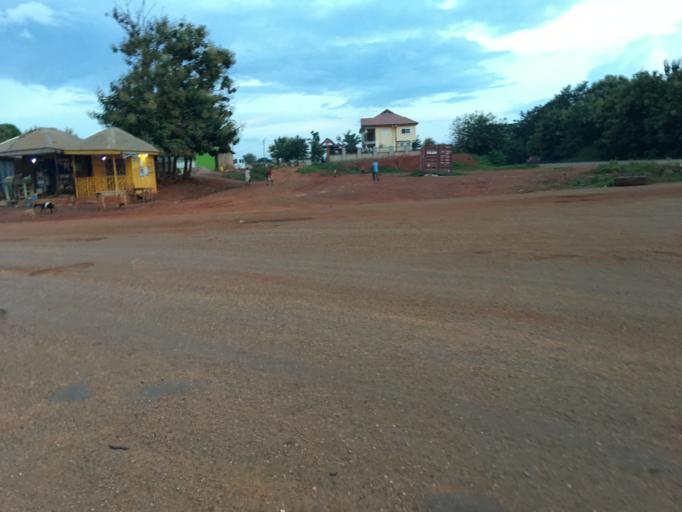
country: GH
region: Western
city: Bibiani
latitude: 6.7875
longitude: -2.5164
